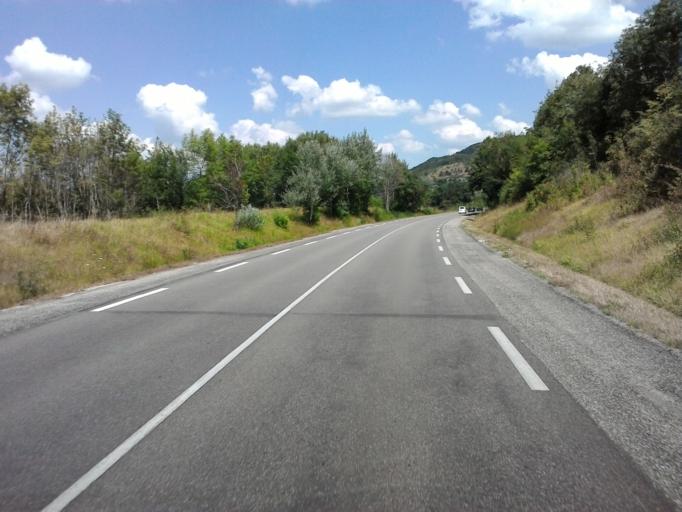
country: FR
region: Franche-Comte
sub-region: Departement du Jura
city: Cousance
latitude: 46.5230
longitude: 5.3899
